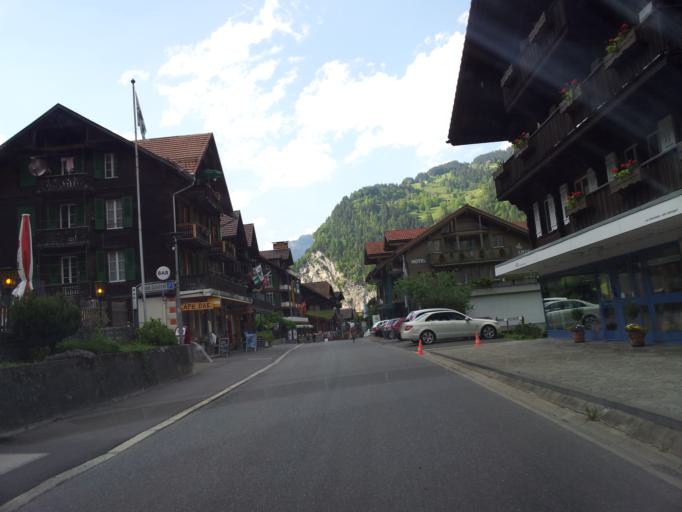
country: CH
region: Bern
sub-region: Interlaken-Oberhasli District
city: Lauterbrunnen
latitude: 46.5947
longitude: 7.9074
